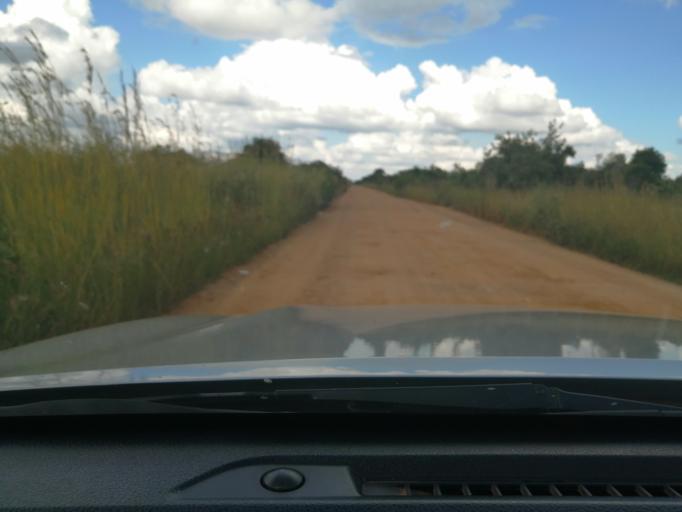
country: ZM
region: Lusaka
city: Lusaka
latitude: -15.2115
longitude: 28.0947
